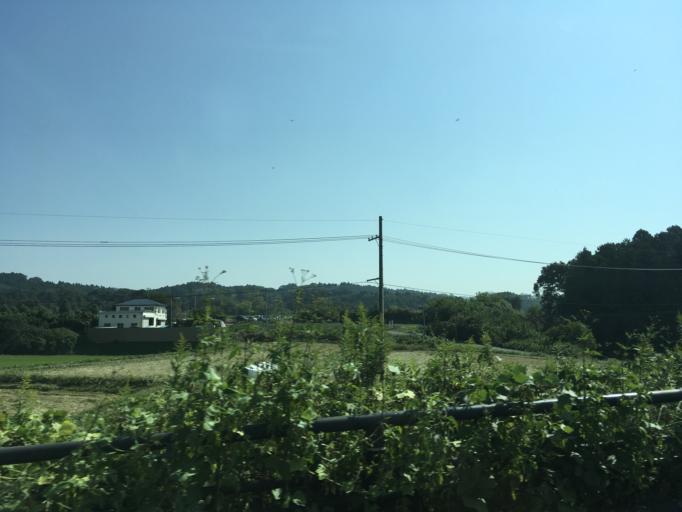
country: JP
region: Miyagi
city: Wakuya
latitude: 38.6749
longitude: 141.2660
